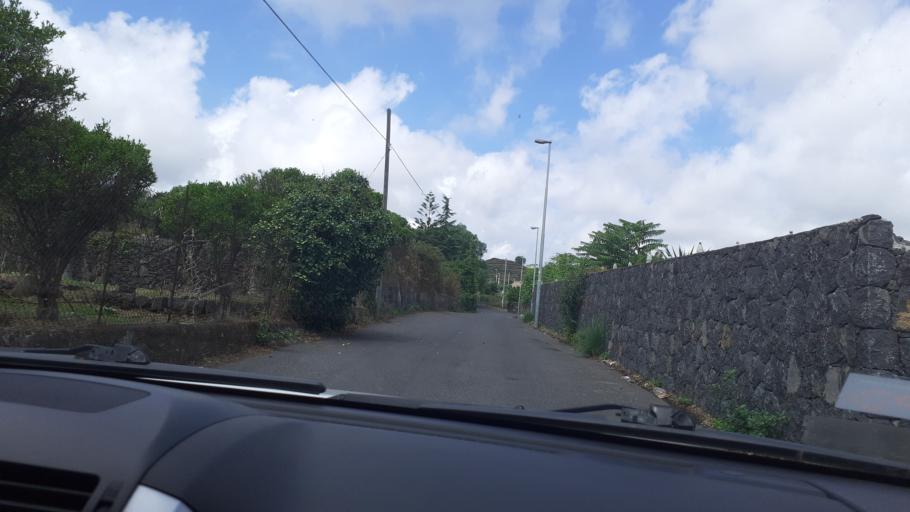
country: IT
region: Sicily
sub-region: Catania
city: San Giovanni la Punta
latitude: 37.5938
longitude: 15.0810
